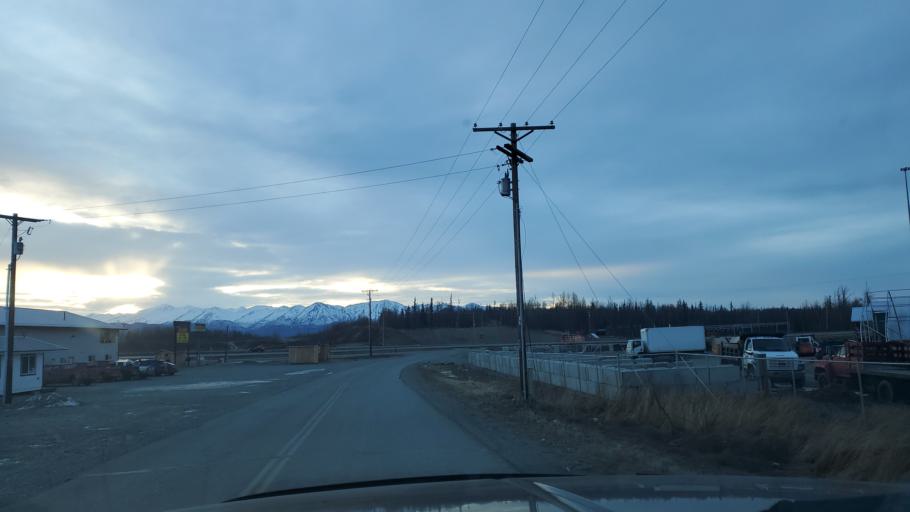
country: US
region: Alaska
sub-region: Matanuska-Susitna Borough
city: Lakes
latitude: 61.5717
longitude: -149.3448
